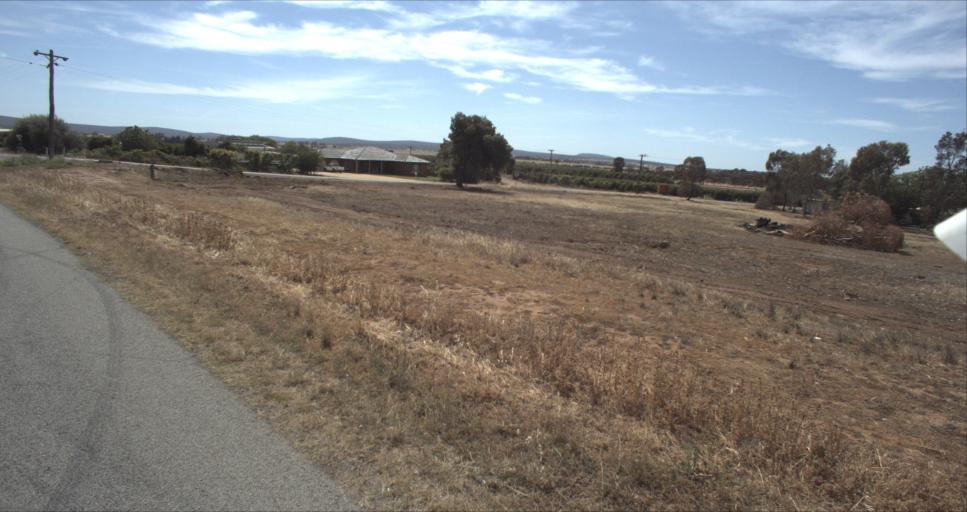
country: AU
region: New South Wales
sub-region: Leeton
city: Leeton
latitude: -34.5704
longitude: 146.4637
